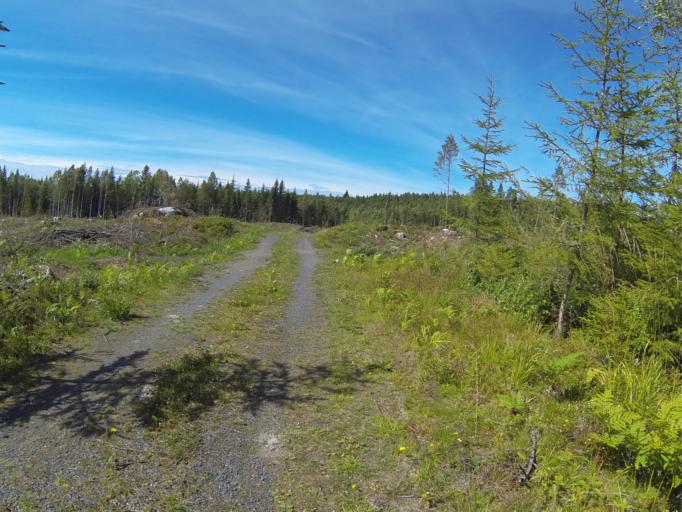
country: FI
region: Varsinais-Suomi
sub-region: Salo
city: Pernioe
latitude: 60.2806
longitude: 23.0535
